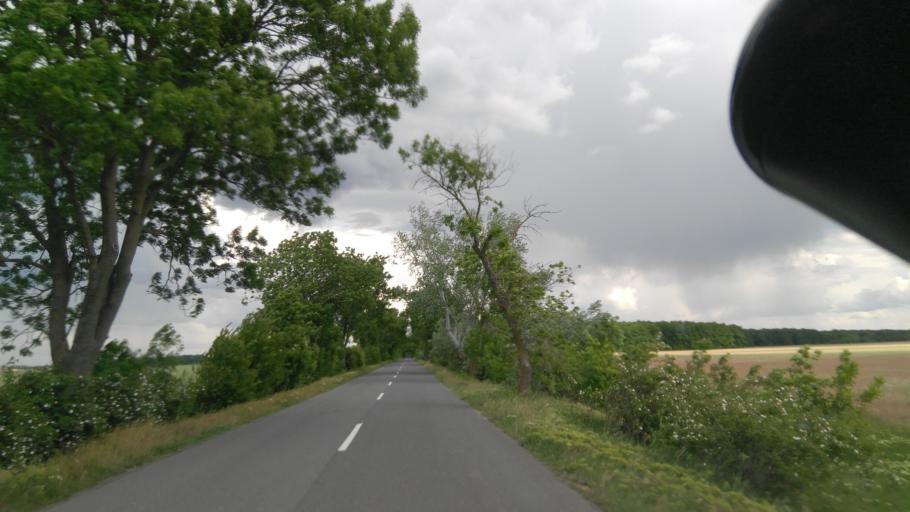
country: HU
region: Bekes
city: Bucsa
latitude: 47.1847
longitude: 21.0405
